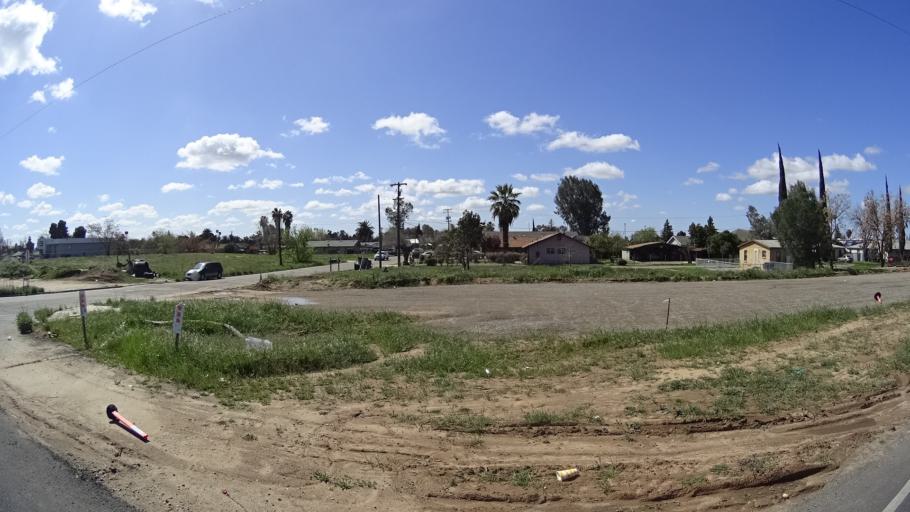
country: US
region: California
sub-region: Fresno County
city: West Park
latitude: 36.8140
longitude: -119.8857
